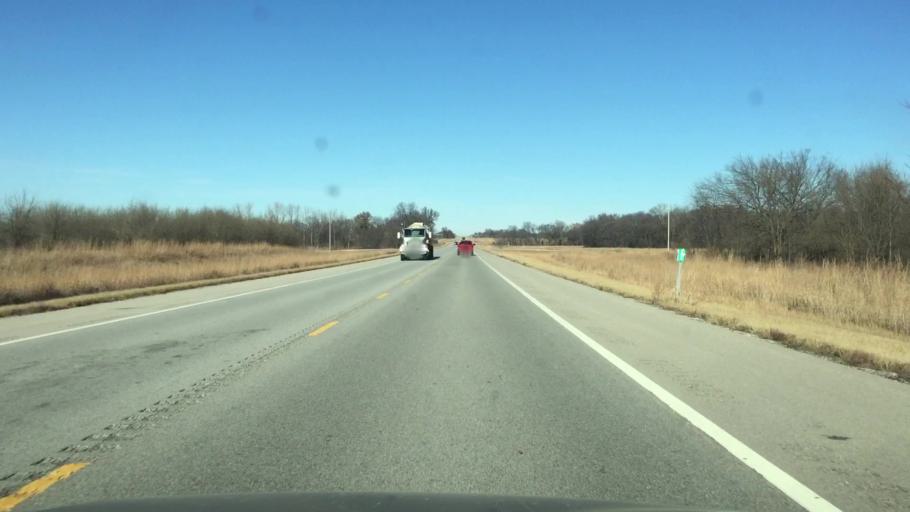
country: US
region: Kansas
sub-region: Allen County
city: Iola
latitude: 37.9781
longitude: -95.3810
